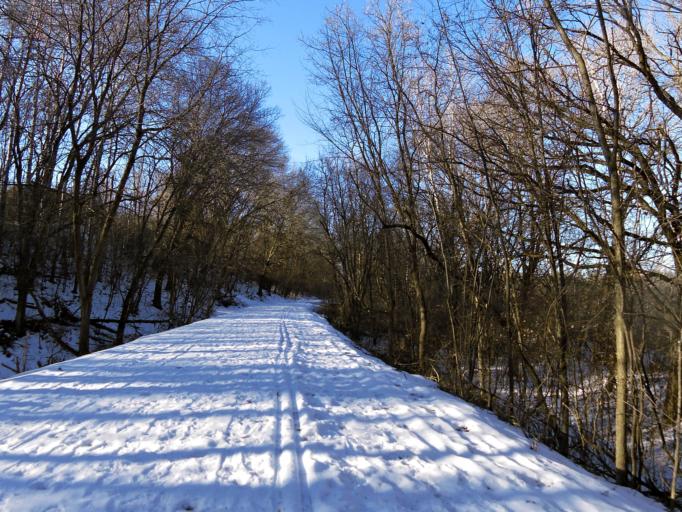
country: US
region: Minnesota
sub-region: Washington County
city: Grant
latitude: 45.0747
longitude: -92.8748
